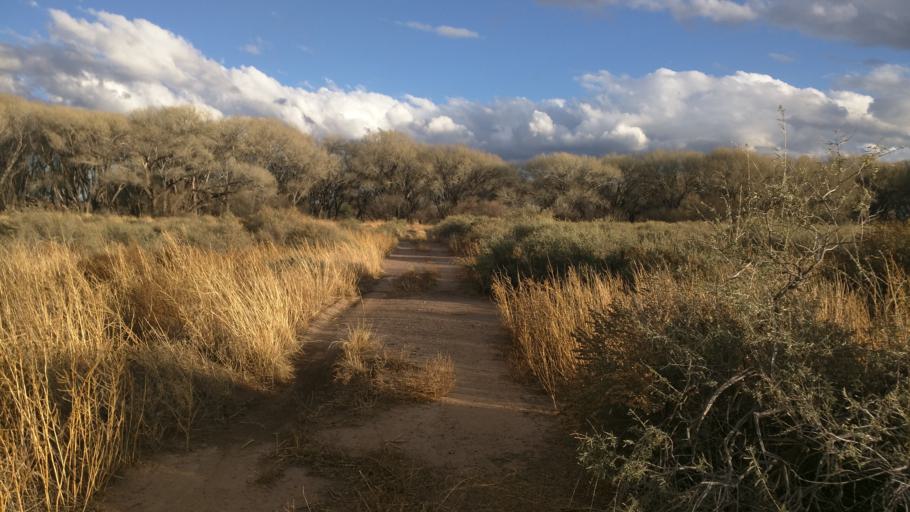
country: US
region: Arizona
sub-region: Cochise County
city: Sierra Vista Southeast
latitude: 31.3685
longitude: -110.1207
